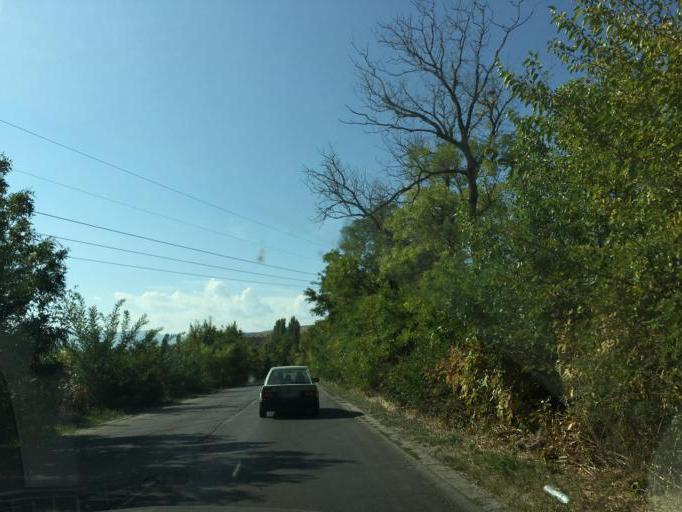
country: BG
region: Pazardzhik
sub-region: Obshtina Pazardzhik
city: Pazardzhik
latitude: 42.1253
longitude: 24.2938
